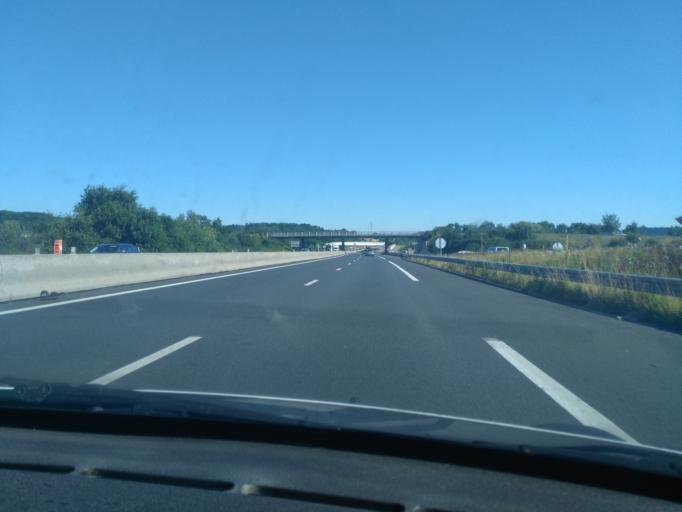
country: FR
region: Rhone-Alpes
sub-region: Departement du Rhone
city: Cailloux-sur-Fontaines
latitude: 45.8613
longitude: 4.9078
